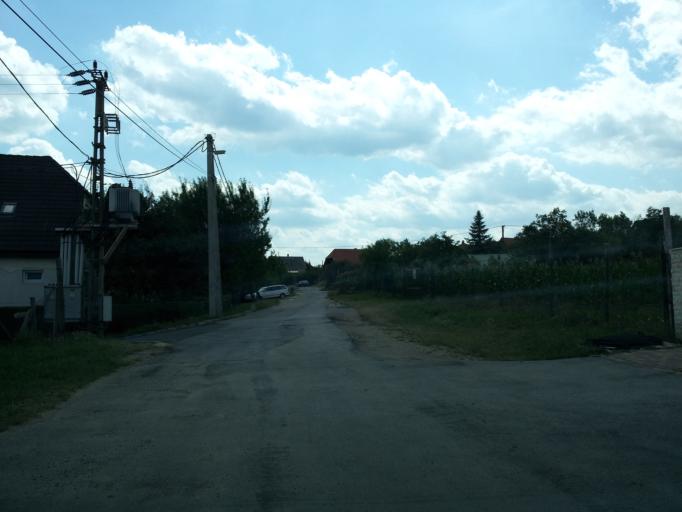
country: HU
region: Veszprem
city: Balatonalmadi
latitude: 47.0534
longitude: 18.0147
